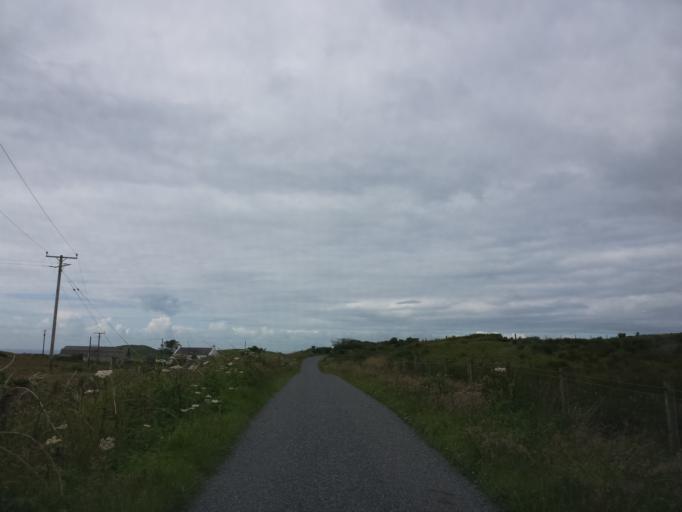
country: GB
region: Scotland
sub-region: Dumfries and Galloway
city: Stranraer
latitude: 54.8844
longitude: -5.1137
